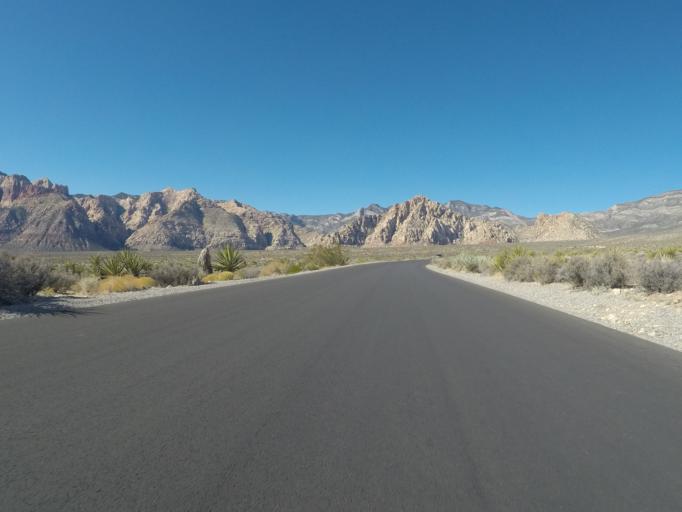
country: US
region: Nevada
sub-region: Clark County
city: Summerlin South
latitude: 36.1595
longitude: -115.4560
